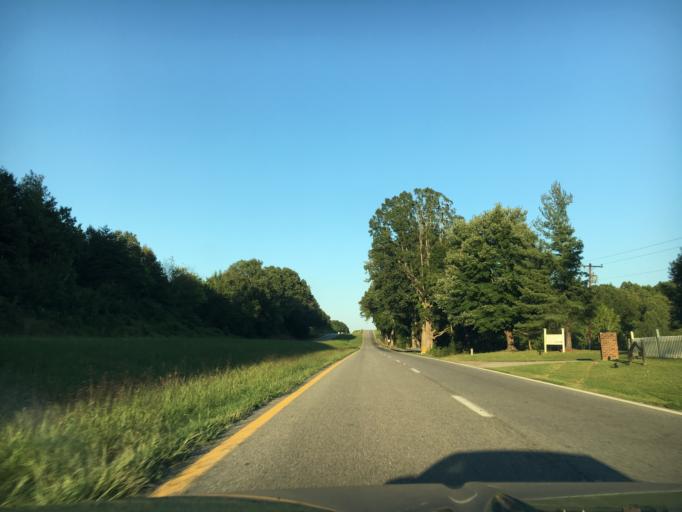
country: US
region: Virginia
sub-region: Halifax County
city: Mountain Road
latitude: 36.5834
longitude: -79.1505
